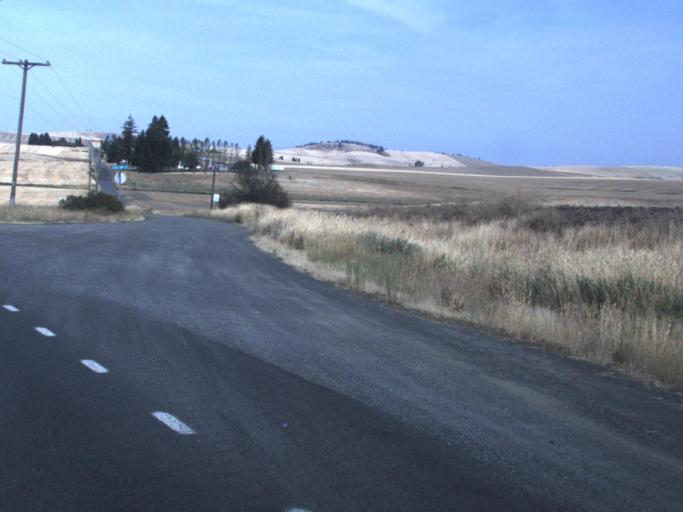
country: US
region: Idaho
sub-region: Benewah County
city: Plummer
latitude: 47.3099
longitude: -117.1638
